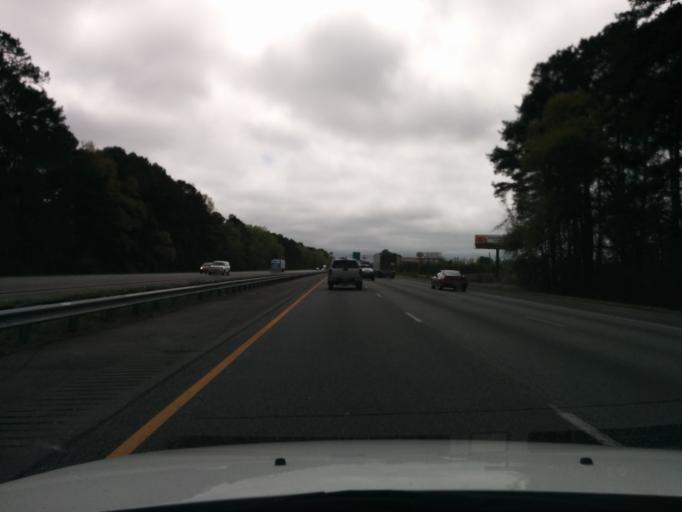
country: US
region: Georgia
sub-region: Chatham County
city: Georgetown
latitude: 32.0161
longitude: -81.2754
